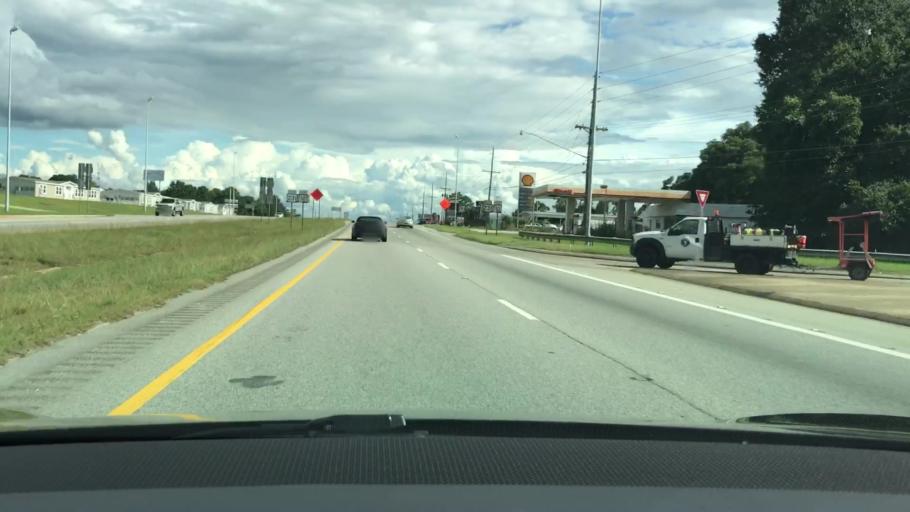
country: US
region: Alabama
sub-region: Pike County
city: Troy
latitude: 31.8058
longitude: -85.9881
